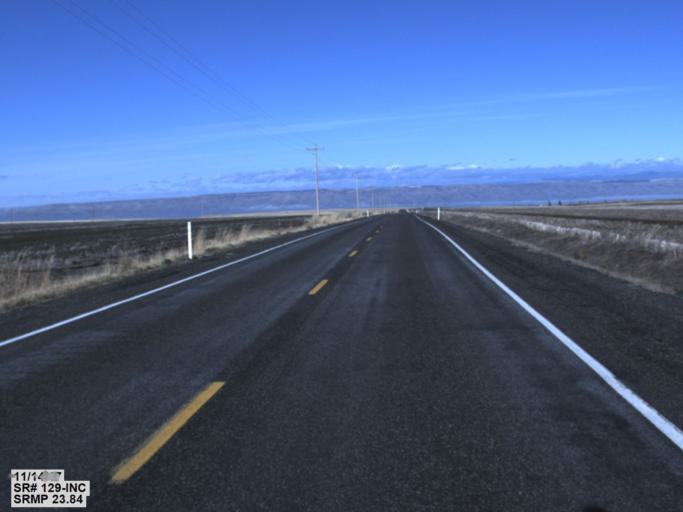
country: US
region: Washington
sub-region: Asotin County
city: Asotin
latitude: 46.2104
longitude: -117.0703
